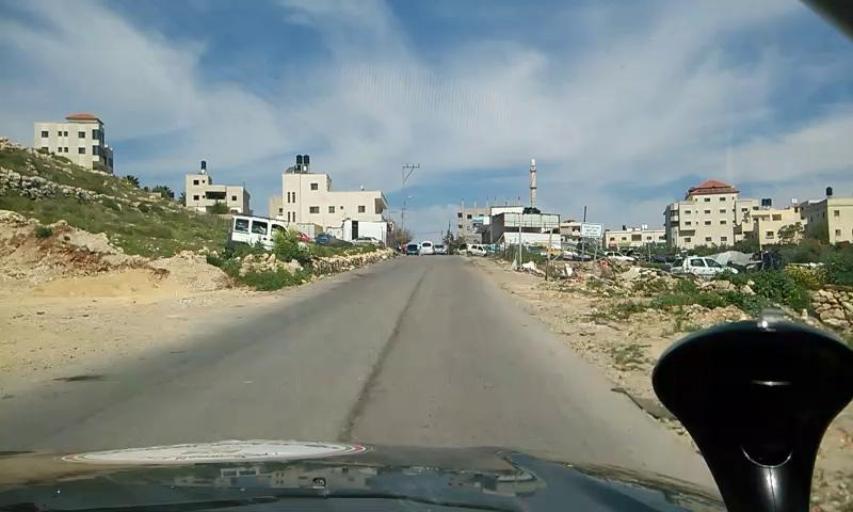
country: PS
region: West Bank
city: Bayt `Ur at Tahta
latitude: 31.8927
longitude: 35.0886
